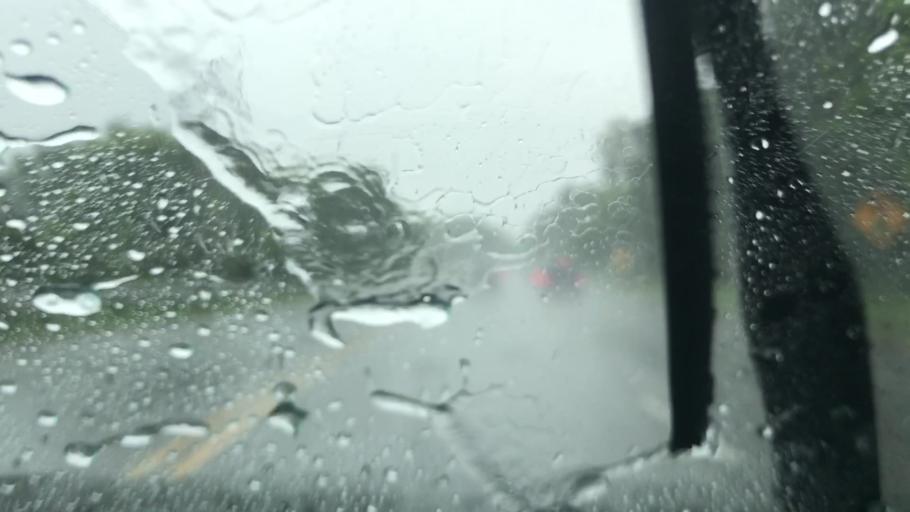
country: US
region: New Jersey
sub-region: Ocean County
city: Toms River
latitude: 39.9849
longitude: -74.1890
